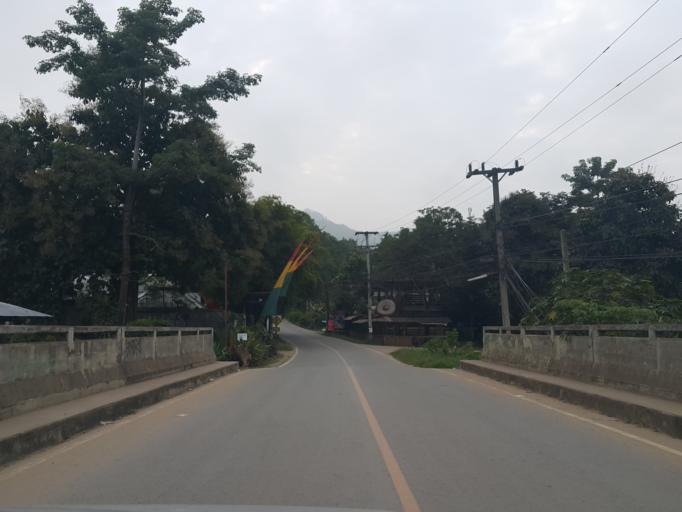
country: TH
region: Chiang Mai
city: Pai
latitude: 19.3561
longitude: 98.4448
